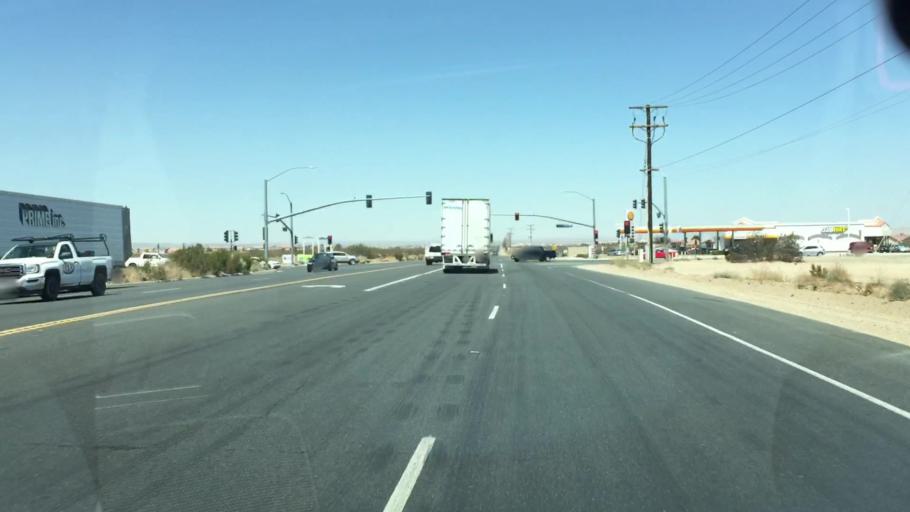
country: US
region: California
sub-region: San Bernardino County
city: Mountain View Acres
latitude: 34.4694
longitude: -117.3994
